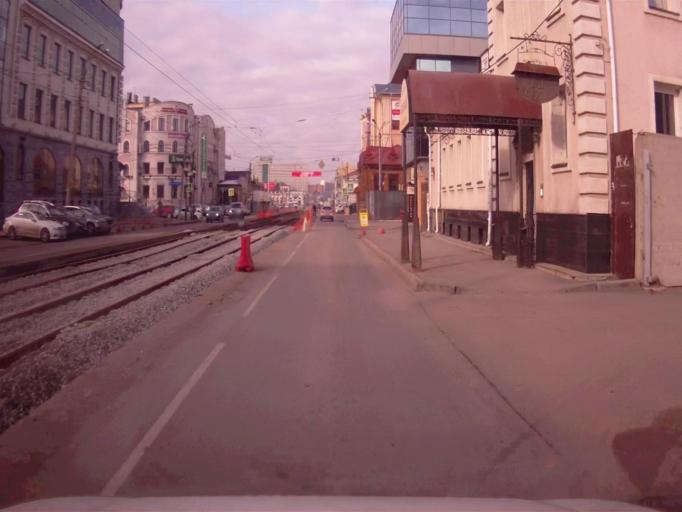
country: RU
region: Chelyabinsk
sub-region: Gorod Chelyabinsk
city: Chelyabinsk
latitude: 55.1681
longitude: 61.4075
